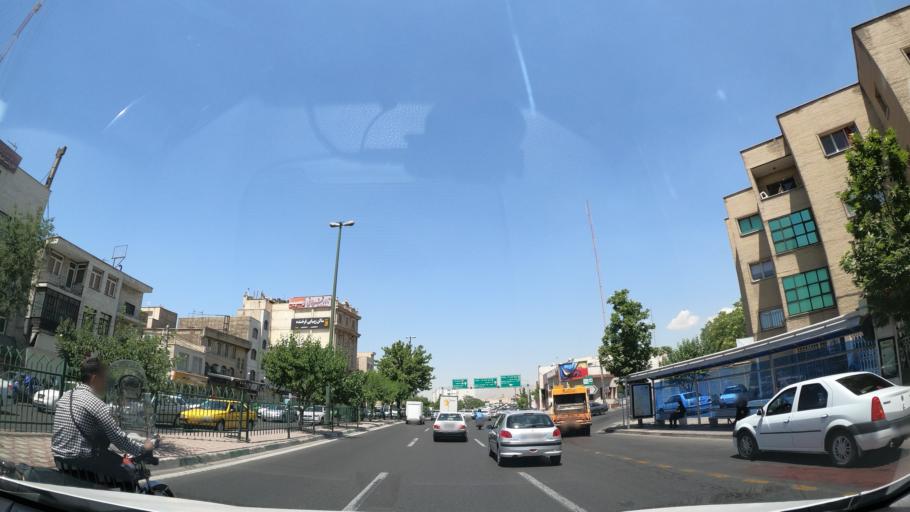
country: IR
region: Tehran
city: Tehran
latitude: 35.7274
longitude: 51.3730
